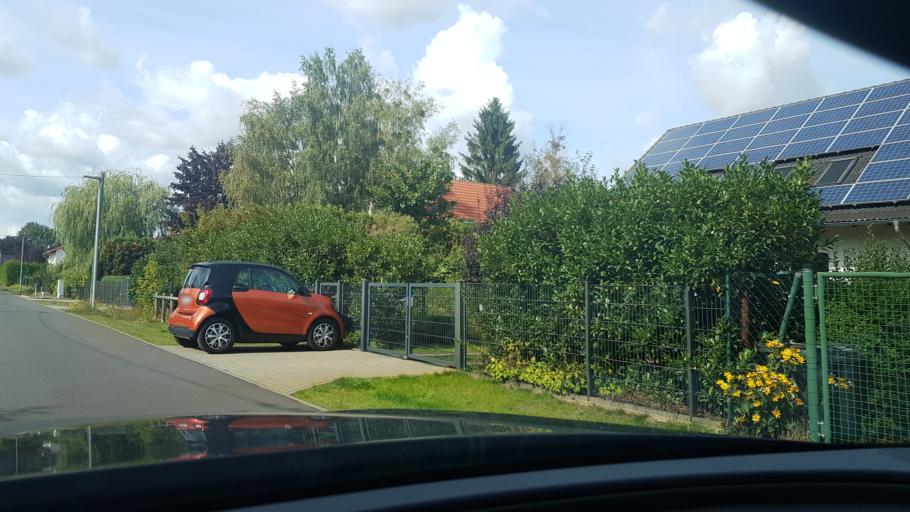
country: DE
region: Brandenburg
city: Brieselang
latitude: 52.5940
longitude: 12.9918
